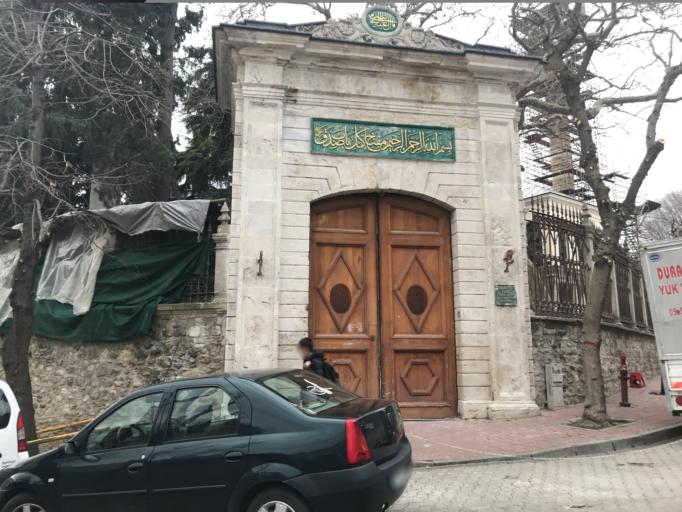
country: TR
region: Istanbul
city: Istanbul
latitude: 41.0218
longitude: 28.9423
